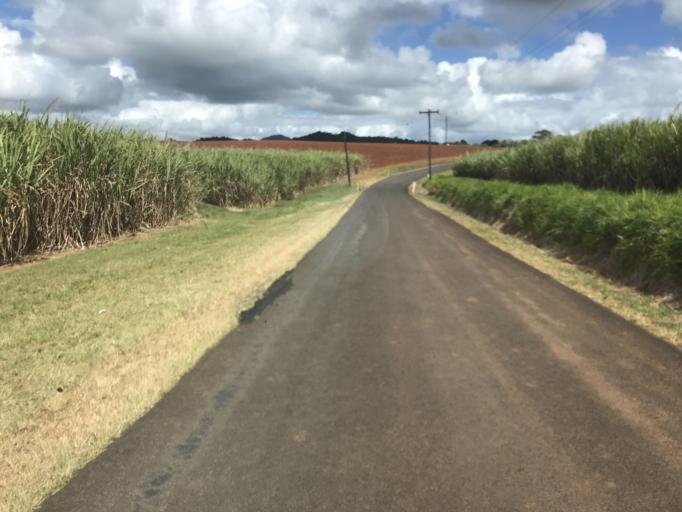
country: AU
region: Queensland
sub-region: Cassowary Coast
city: Innisfail
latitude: -17.5564
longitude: 145.8922
